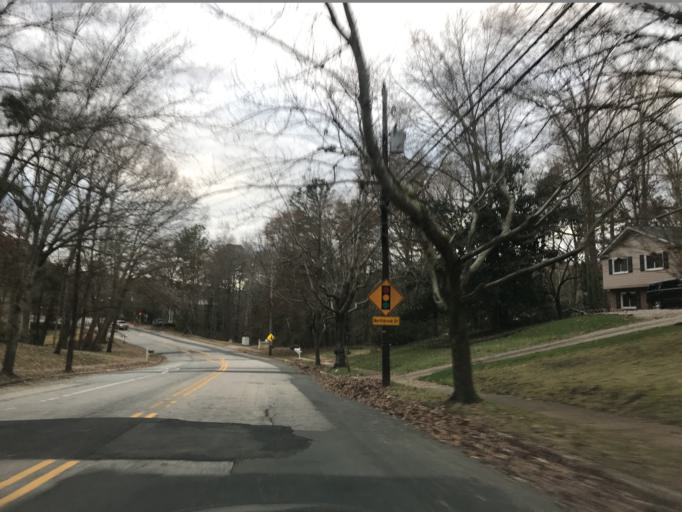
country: US
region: North Carolina
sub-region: Wake County
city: West Raleigh
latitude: 35.8455
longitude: -78.6609
